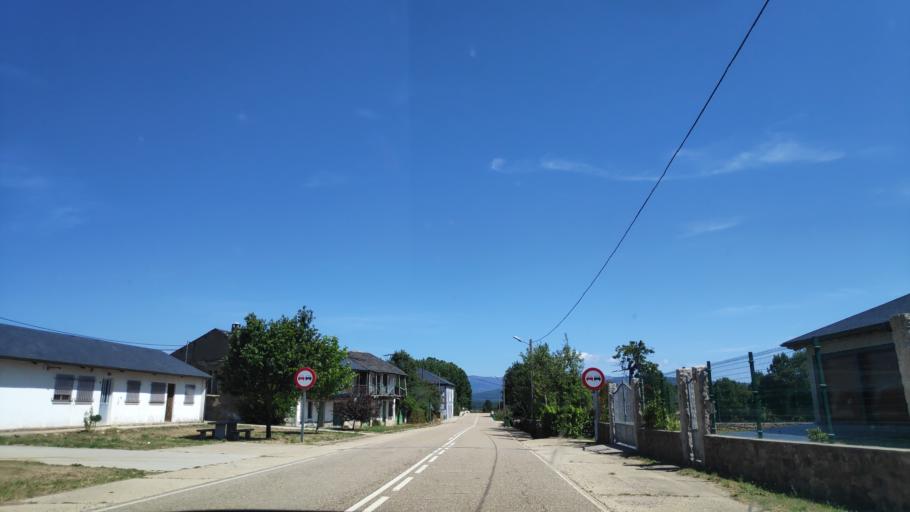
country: ES
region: Castille and Leon
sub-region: Provincia de Zamora
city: Puebla de Sanabria
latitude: 42.0397
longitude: -6.6665
